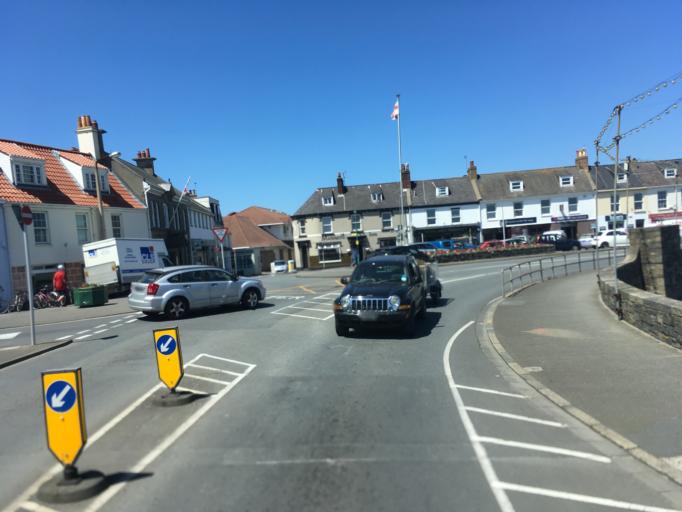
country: GG
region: St Peter Port
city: Saint Peter Port
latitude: 49.4827
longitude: -2.5194
